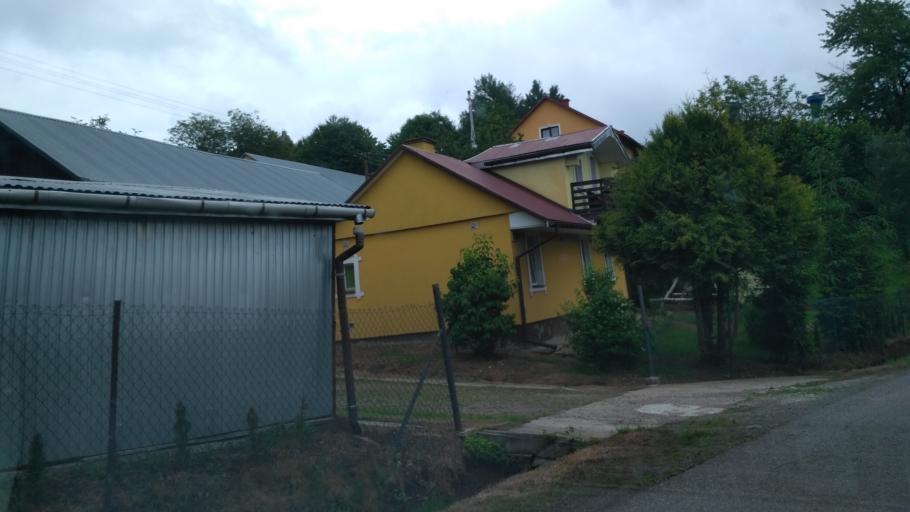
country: PL
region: Subcarpathian Voivodeship
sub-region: Powiat przemyski
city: Nienadowa
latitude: 49.8619
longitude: 22.4090
